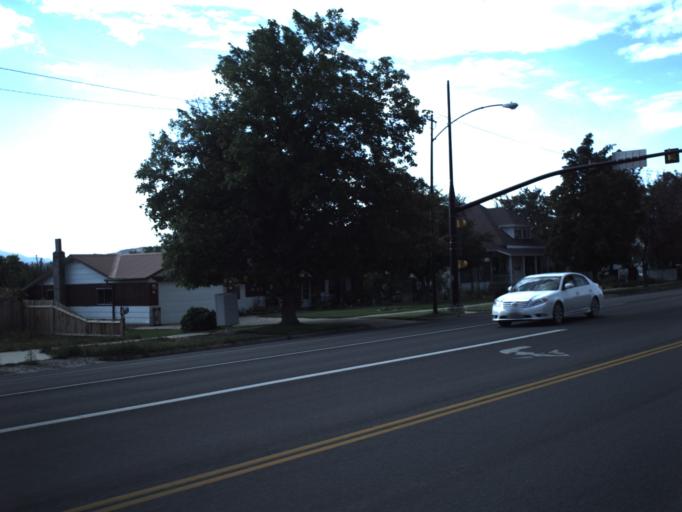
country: US
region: Utah
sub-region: Sanpete County
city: Mount Pleasant
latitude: 39.5397
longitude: -111.4552
